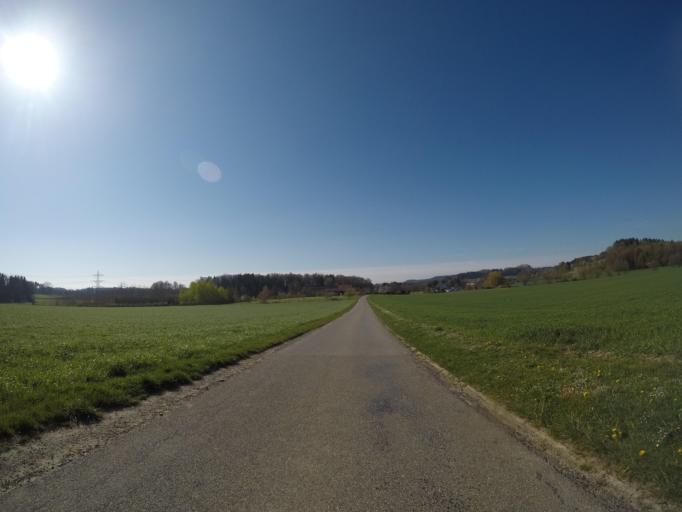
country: DE
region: Baden-Wuerttemberg
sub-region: Tuebingen Region
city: Ebenweiler
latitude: 47.8920
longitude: 9.5242
